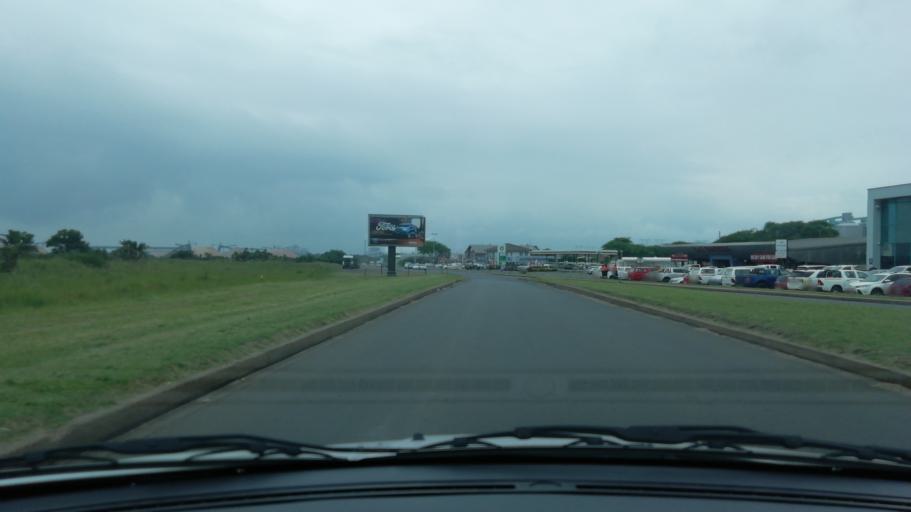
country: ZA
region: KwaZulu-Natal
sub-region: uThungulu District Municipality
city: Richards Bay
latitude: -28.7580
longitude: 32.0447
